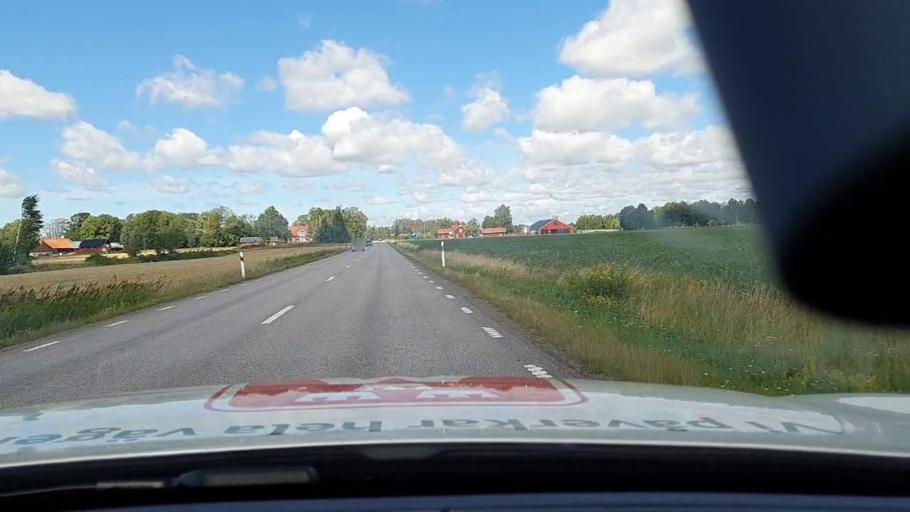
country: SE
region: Vaestra Goetaland
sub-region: Skovde Kommun
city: Stopen
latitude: 58.5468
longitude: 14.0020
